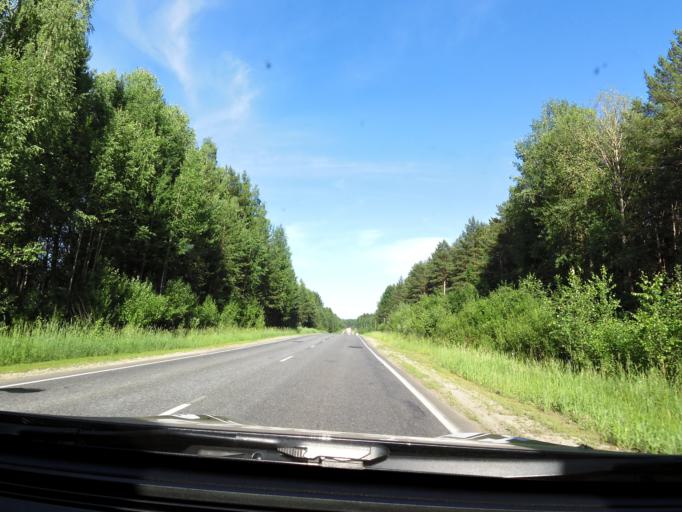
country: RU
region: Kirov
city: Belaya Kholunitsa
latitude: 58.8950
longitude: 50.9005
